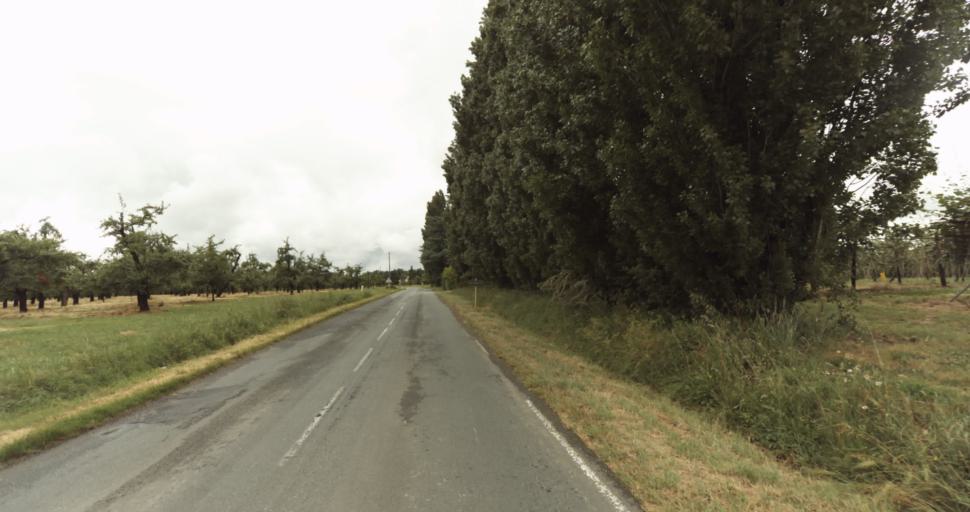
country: FR
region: Aquitaine
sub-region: Departement de la Dordogne
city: Beaumont-du-Perigord
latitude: 44.7381
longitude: 0.7825
